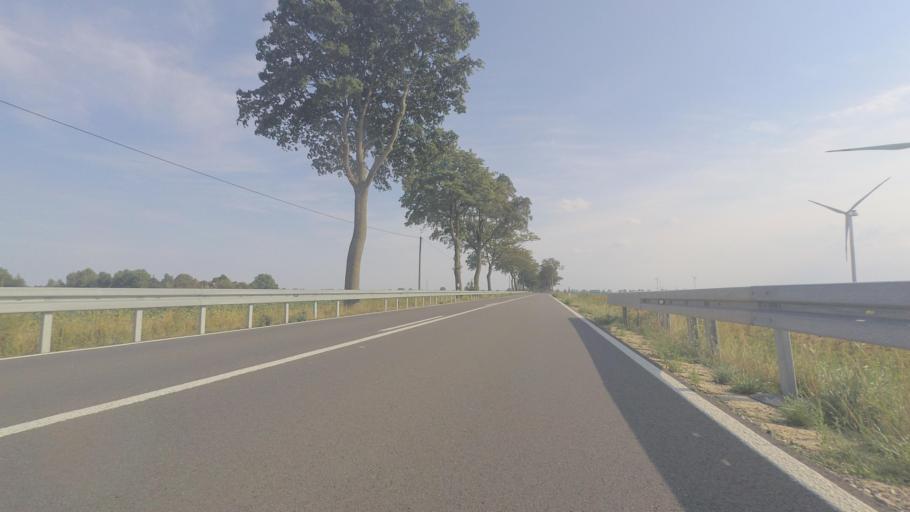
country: DE
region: Mecklenburg-Vorpommern
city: Gormin
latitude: 54.0119
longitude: 13.1407
